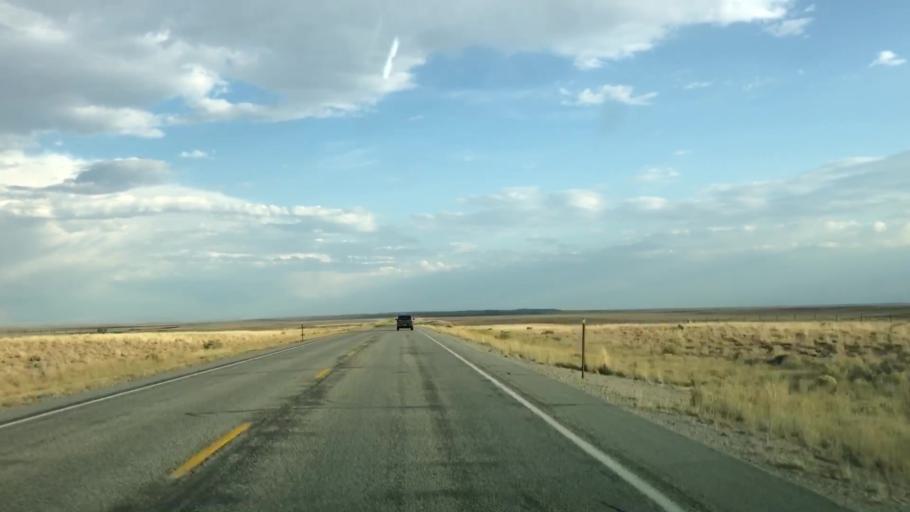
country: US
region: Wyoming
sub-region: Sublette County
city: Marbleton
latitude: 42.3344
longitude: -109.5186
